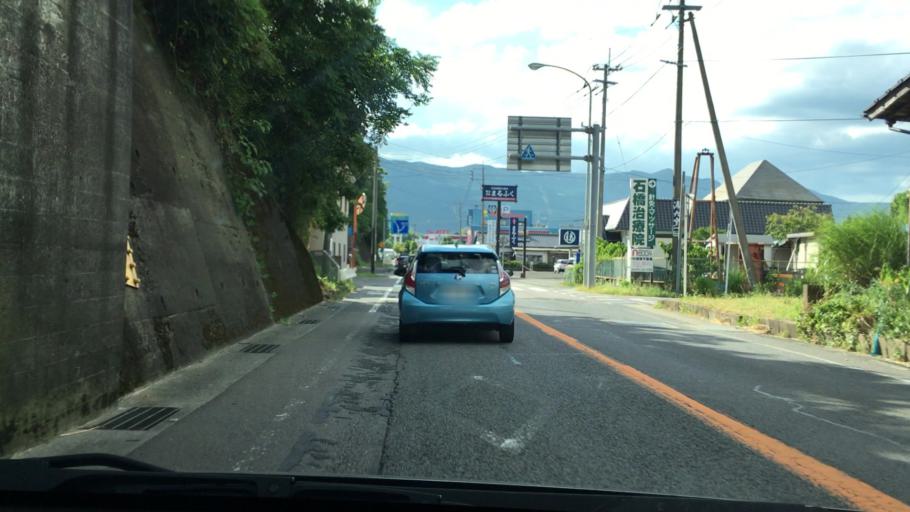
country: JP
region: Saga Prefecture
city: Imaricho-ko
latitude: 33.1881
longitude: 129.8645
